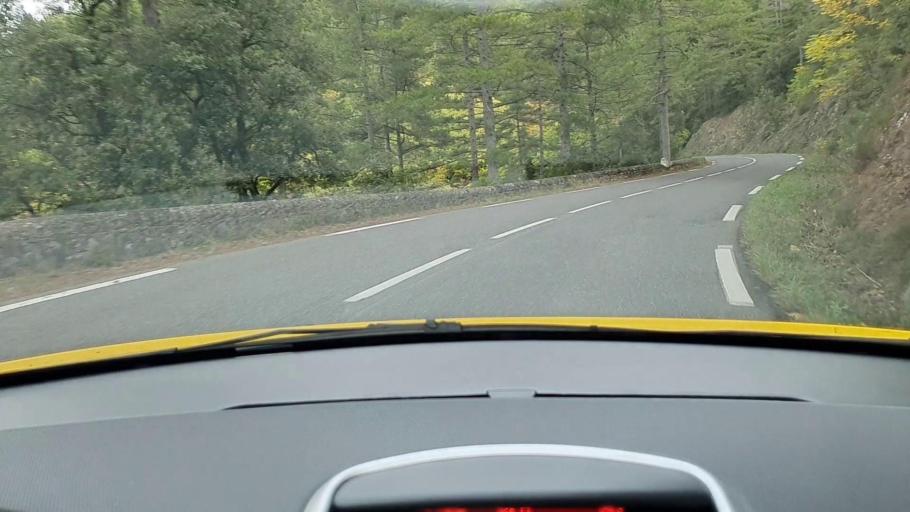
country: FR
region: Languedoc-Roussillon
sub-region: Departement du Gard
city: Le Vigan
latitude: 44.0098
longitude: 3.5946
